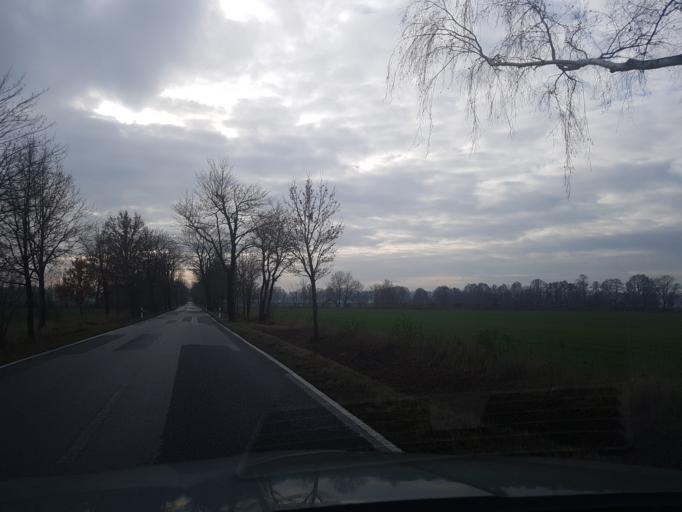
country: DE
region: Brandenburg
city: Hirschfeld
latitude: 51.4187
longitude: 13.6222
